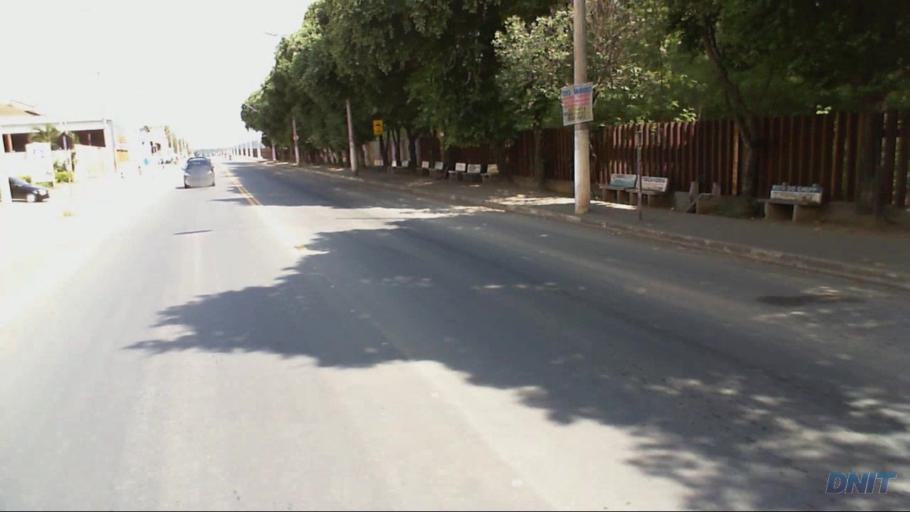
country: BR
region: Minas Gerais
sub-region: Governador Valadares
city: Governador Valadares
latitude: -18.8892
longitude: -41.9732
